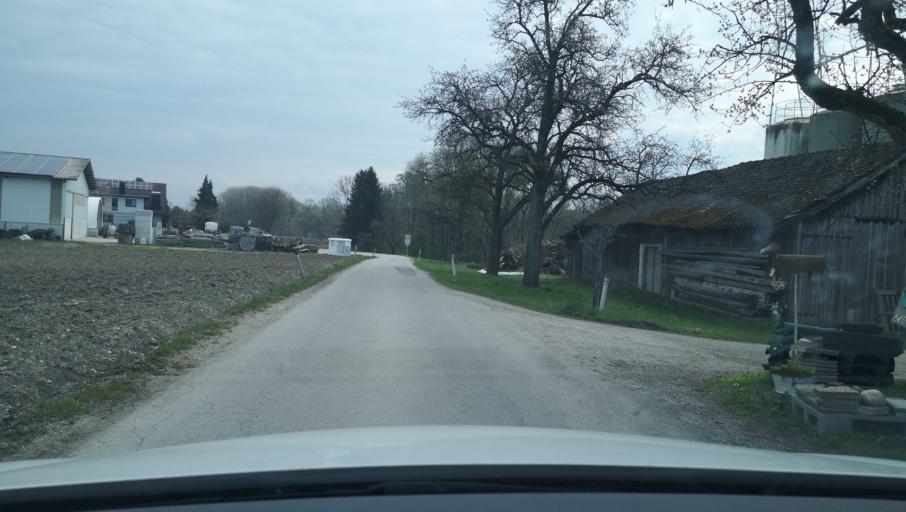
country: AT
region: Lower Austria
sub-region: Politischer Bezirk Amstetten
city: Amstetten
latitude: 48.1124
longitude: 14.8915
